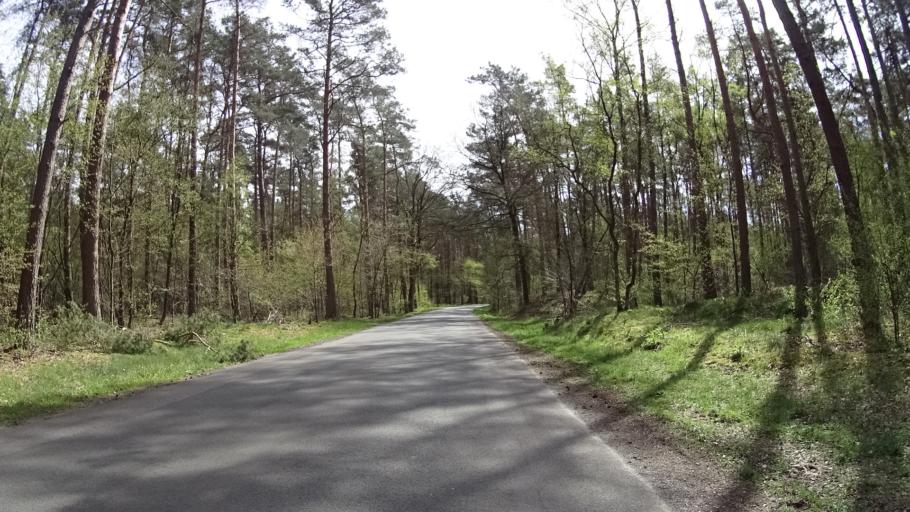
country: DE
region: Lower Saxony
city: Emsburen
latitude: 52.4361
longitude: 7.3490
